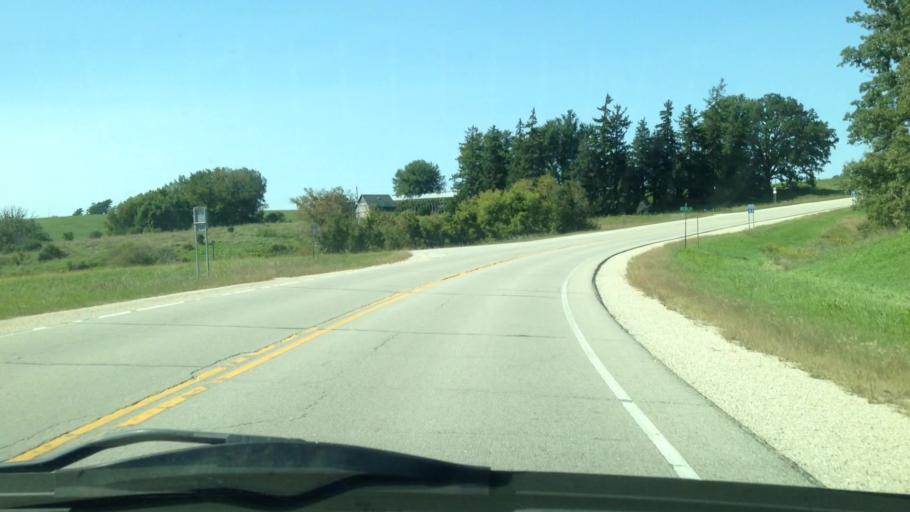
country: US
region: Minnesota
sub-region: Houston County
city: Spring Grove
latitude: 43.6024
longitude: -91.7890
